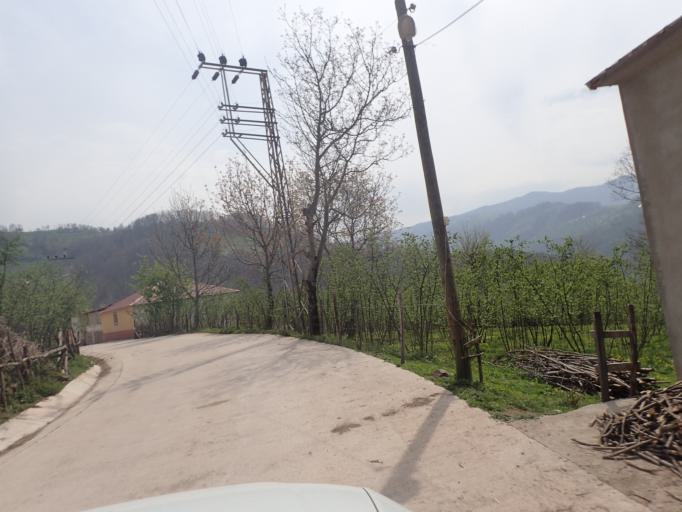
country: TR
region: Ordu
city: Aybasti
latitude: 40.7127
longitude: 37.2842
